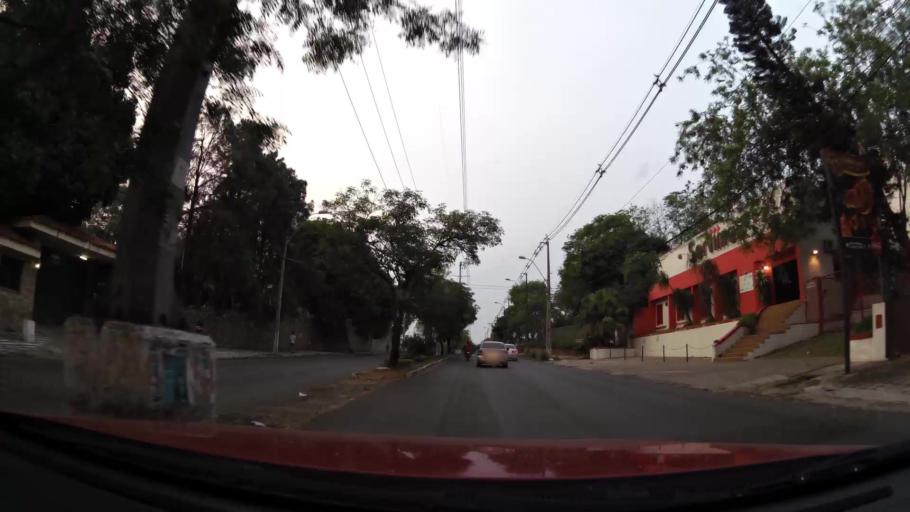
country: PY
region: Asuncion
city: Asuncion
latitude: -25.3232
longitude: -57.6281
